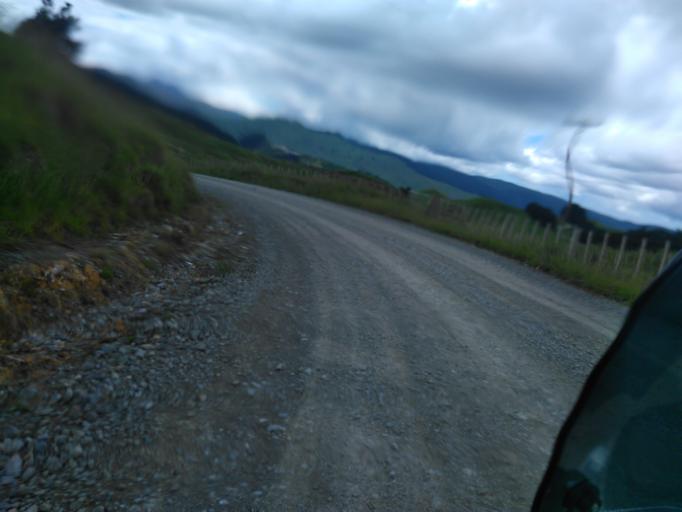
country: NZ
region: Gisborne
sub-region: Gisborne District
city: Gisborne
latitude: -38.0467
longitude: 178.0587
